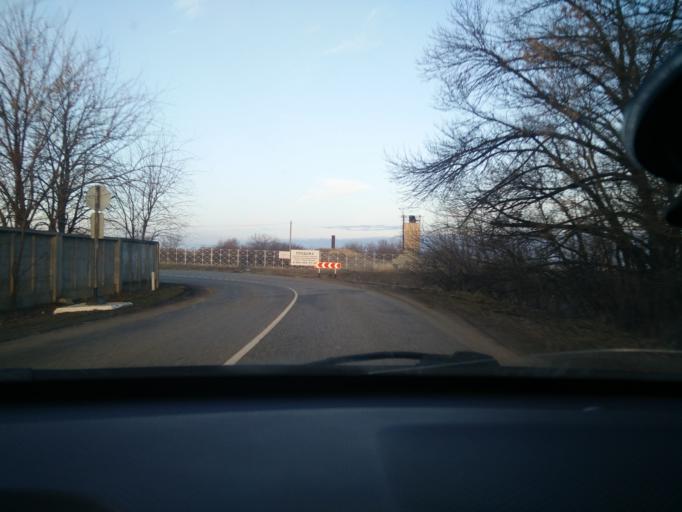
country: RU
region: Stavropol'skiy
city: Balakhonovskoye
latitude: 44.9802
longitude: 41.6898
